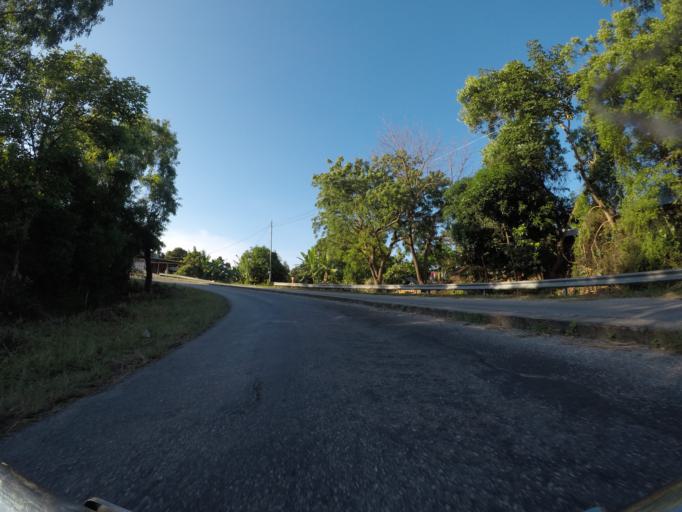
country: TZ
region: Pemba South
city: Uwelini
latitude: -5.3757
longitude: 39.6739
